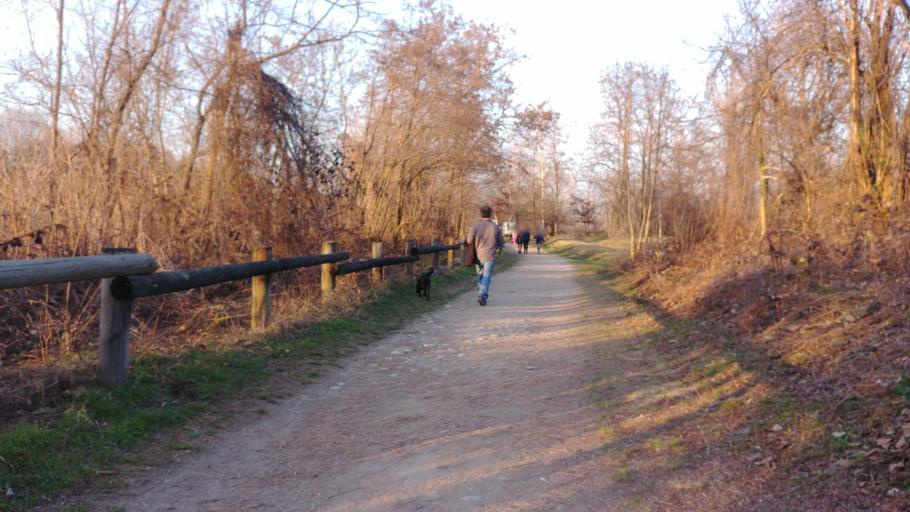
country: IT
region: Piedmont
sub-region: Provincia di Cuneo
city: Cuneo
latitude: 44.3647
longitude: 7.5392
